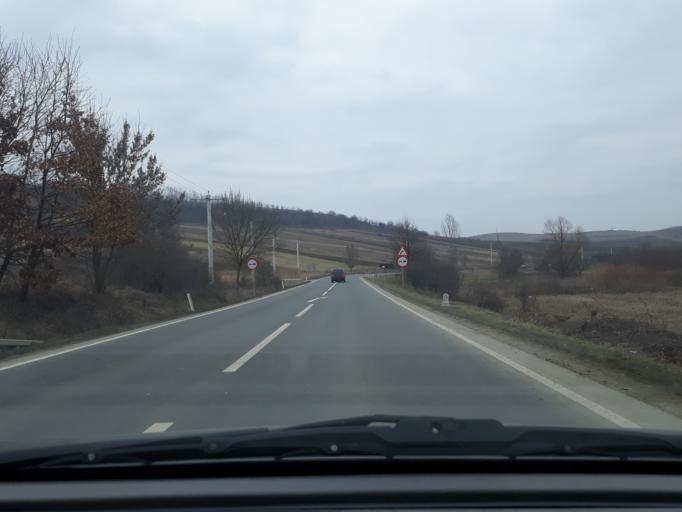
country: RO
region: Salaj
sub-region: Comuna Nusfalau
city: Nusfalau
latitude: 47.2145
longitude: 22.7219
